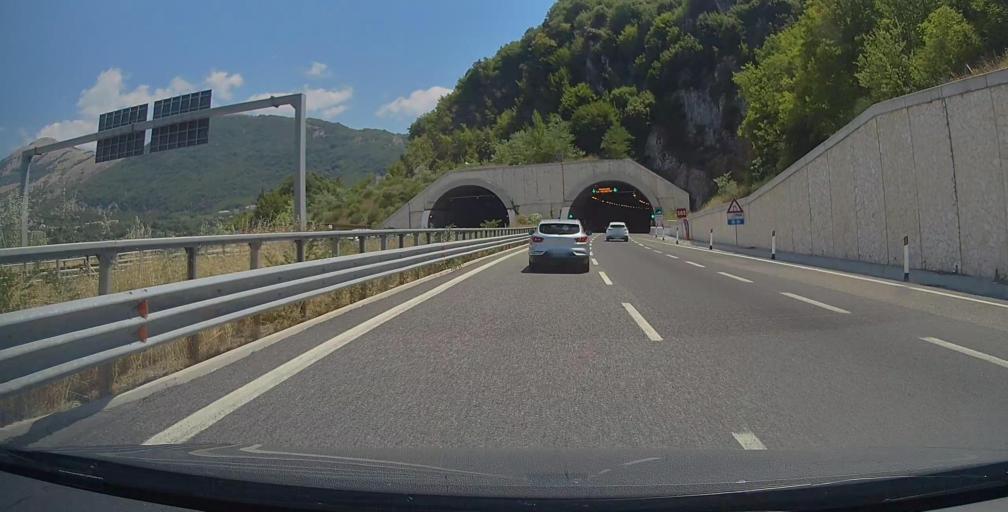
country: IT
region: Calabria
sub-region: Provincia di Cosenza
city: Mormanno
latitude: 39.8993
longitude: 15.9764
